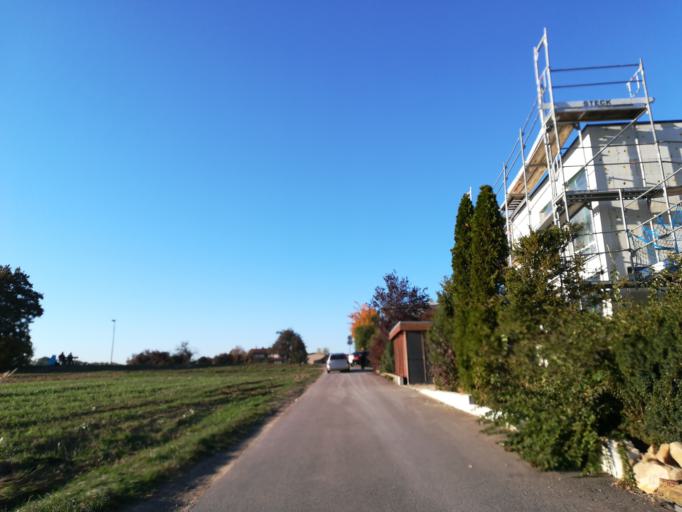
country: DE
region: Baden-Wuerttemberg
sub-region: Regierungsbezirk Stuttgart
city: Filderstadt
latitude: 48.6802
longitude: 9.2384
